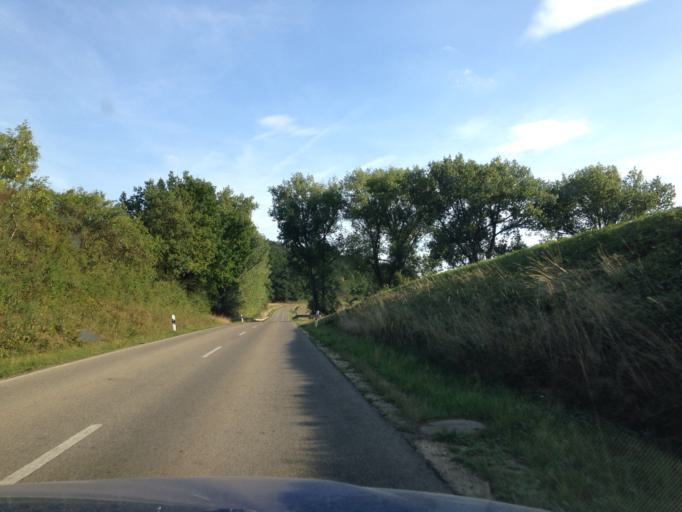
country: DE
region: Bavaria
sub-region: Regierungsbezirk Mittelfranken
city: Thalmassing
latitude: 49.1249
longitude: 11.2119
